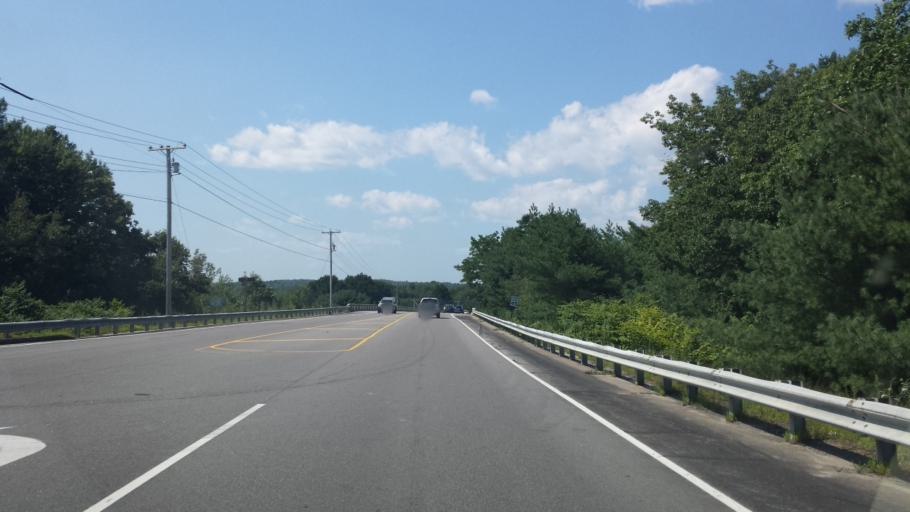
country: US
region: Maine
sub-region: York County
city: Biddeford
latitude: 43.4719
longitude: -70.4896
